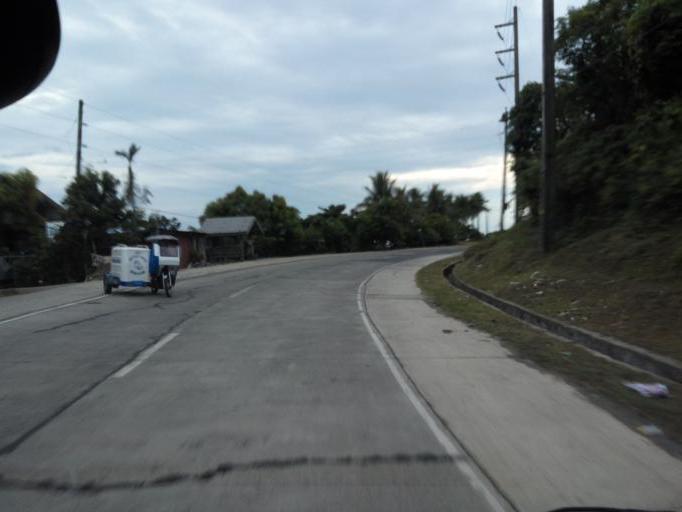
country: PH
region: Cagayan Valley
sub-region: Province of Cagayan
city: Casambalangan
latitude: 18.3961
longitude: 122.1281
